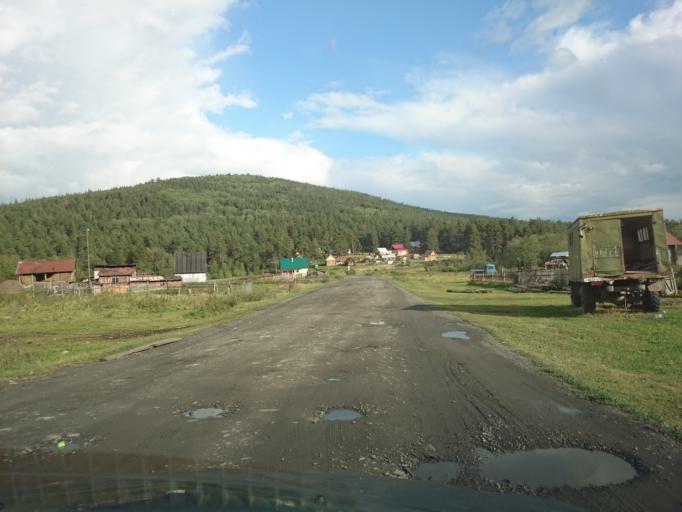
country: RU
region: Bashkortostan
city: Beloretsk
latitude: 54.0474
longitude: 58.3279
